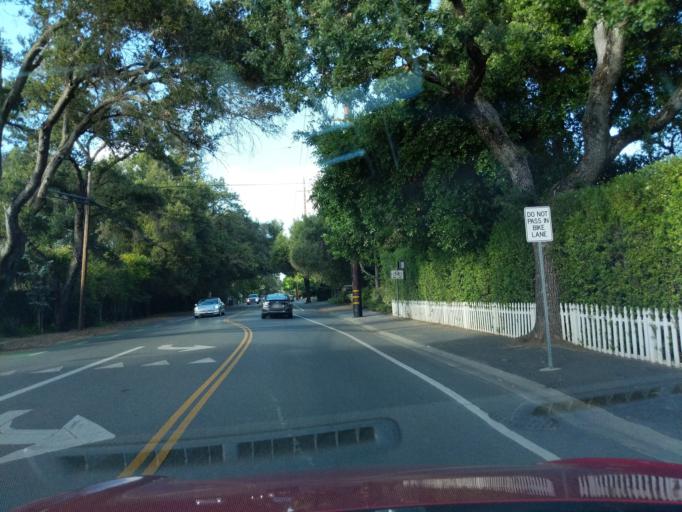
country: US
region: California
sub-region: San Mateo County
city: West Menlo Park
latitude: 37.4410
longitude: -122.2000
